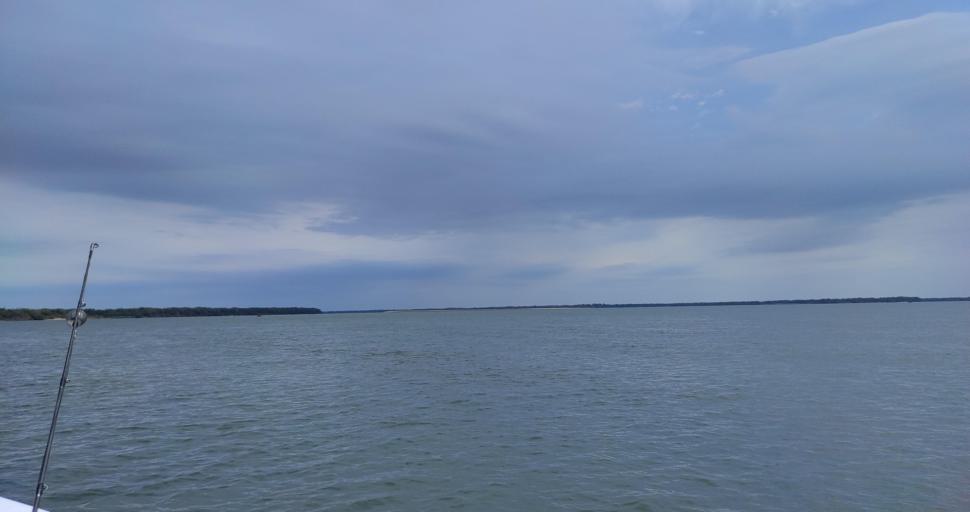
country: PY
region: Neembucu
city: Cerrito
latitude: -27.3460
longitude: -57.6902
